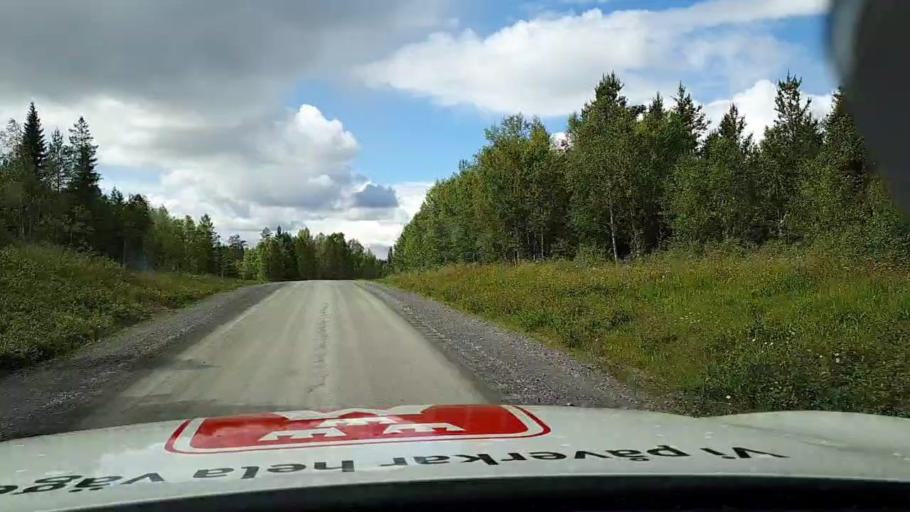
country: SE
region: Jaemtland
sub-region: Krokoms Kommun
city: Valla
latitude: 63.6770
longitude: 13.6853
